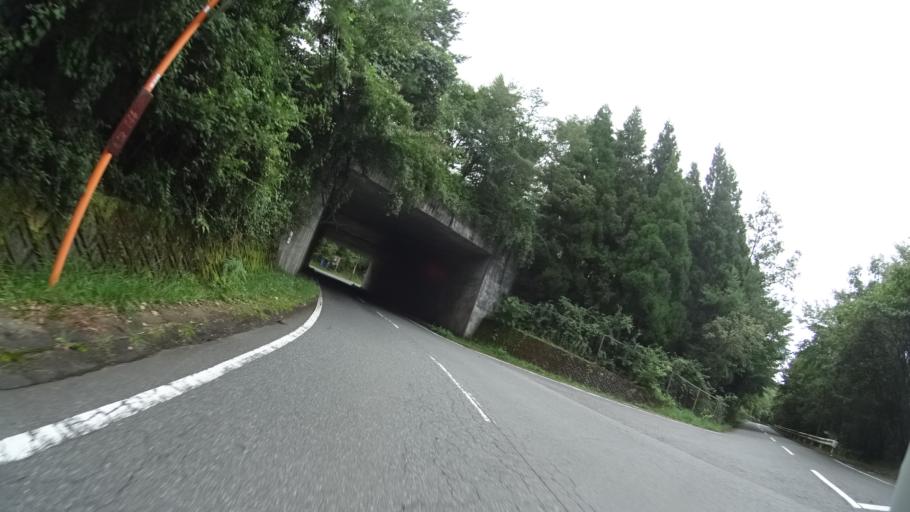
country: JP
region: Oita
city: Beppu
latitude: 33.2961
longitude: 131.3760
